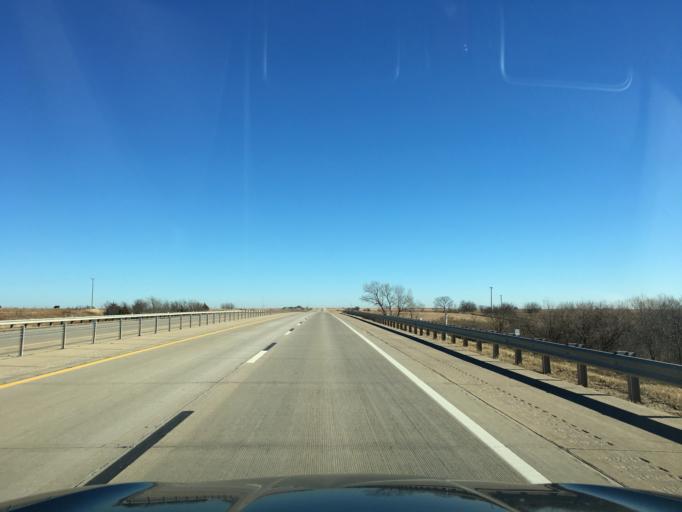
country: US
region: Oklahoma
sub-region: Noble County
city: Perry
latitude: 36.3920
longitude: -97.1423
